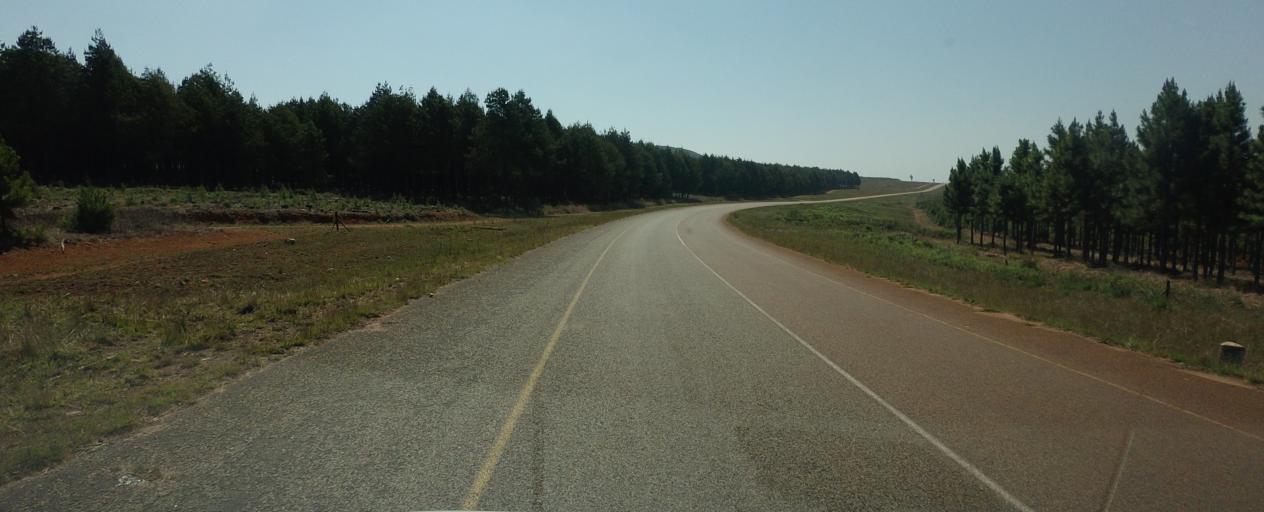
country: ZA
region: Mpumalanga
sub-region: Ehlanzeni District
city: Graksop
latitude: -24.7849
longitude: 30.8652
